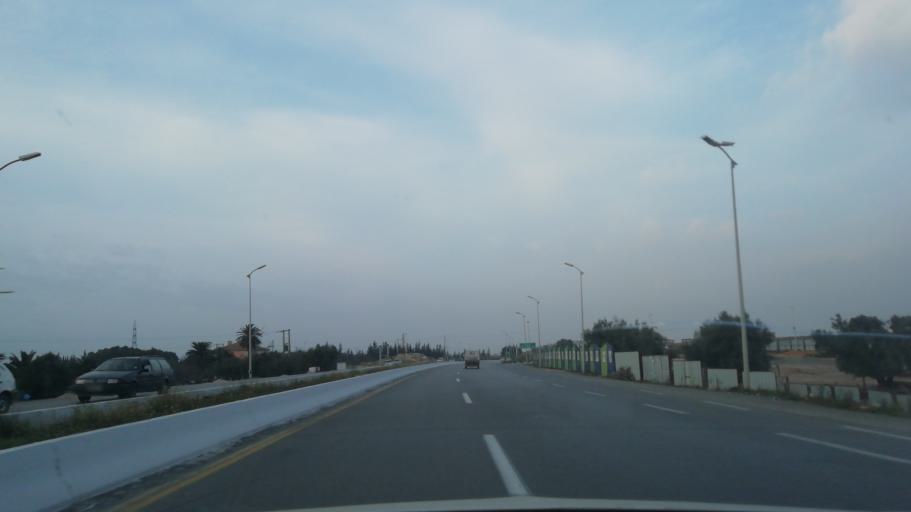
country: DZ
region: Sidi Bel Abbes
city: Sidi Bel Abbes
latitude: 35.2056
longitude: -0.6594
